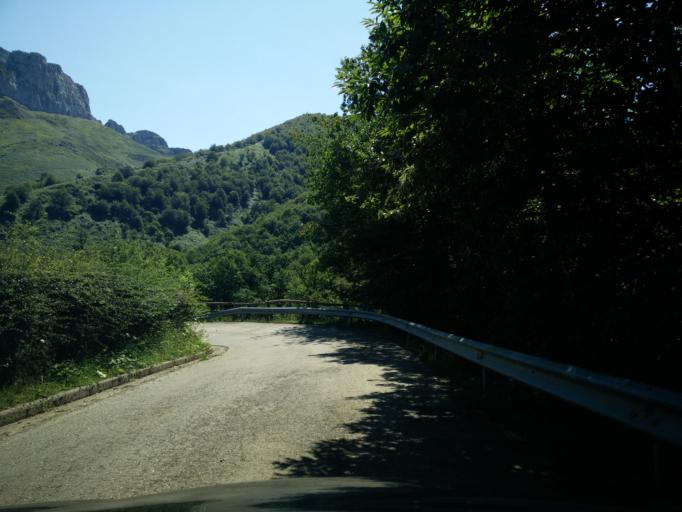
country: ES
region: Asturias
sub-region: Province of Asturias
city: Amieva
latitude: 43.1938
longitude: -5.1256
